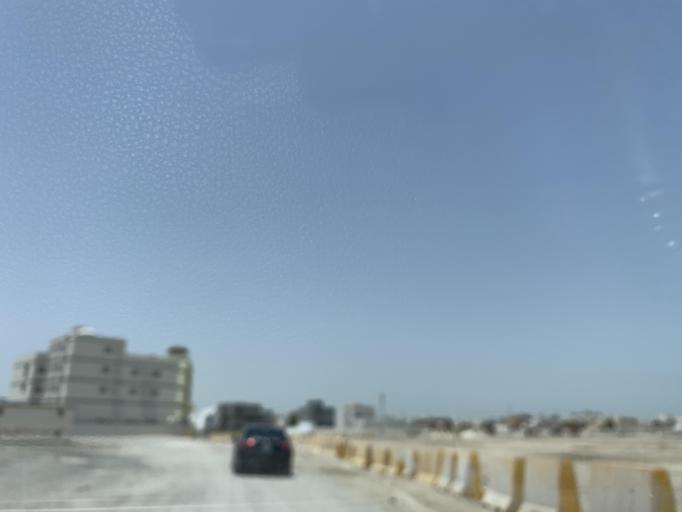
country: BH
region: Northern
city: Sitrah
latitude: 26.1432
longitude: 50.5937
